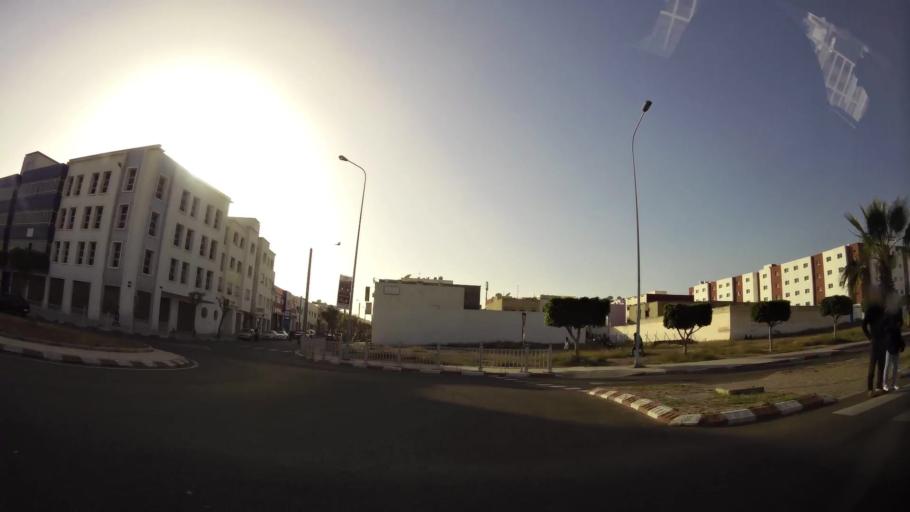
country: MA
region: Oued ed Dahab-Lagouira
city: Dakhla
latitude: 30.4120
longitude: -9.5463
